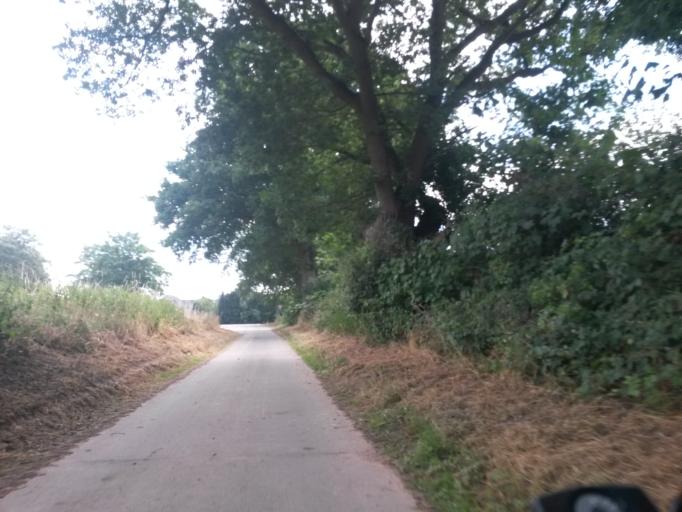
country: DE
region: North Rhine-Westphalia
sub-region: Regierungsbezirk Dusseldorf
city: Rheurdt
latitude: 51.4325
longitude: 6.4803
